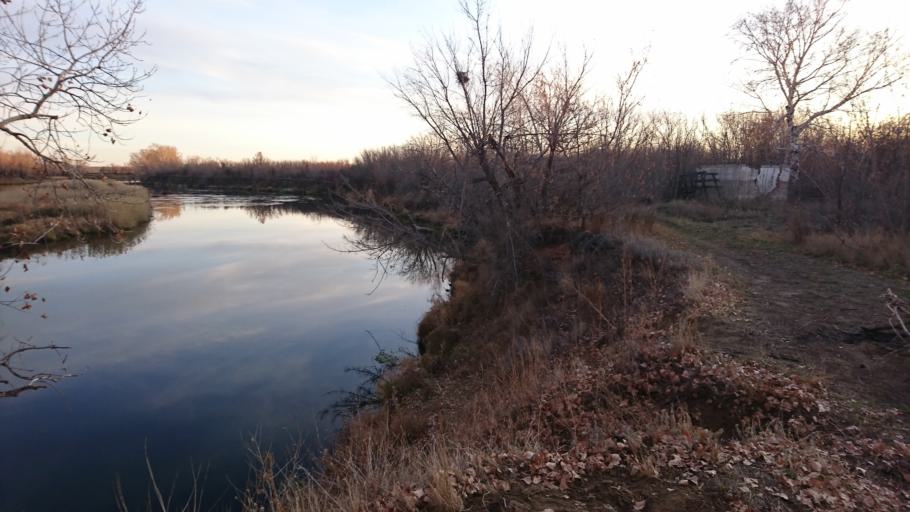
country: RU
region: Orenburg
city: Novotroitsk
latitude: 51.1589
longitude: 58.3134
